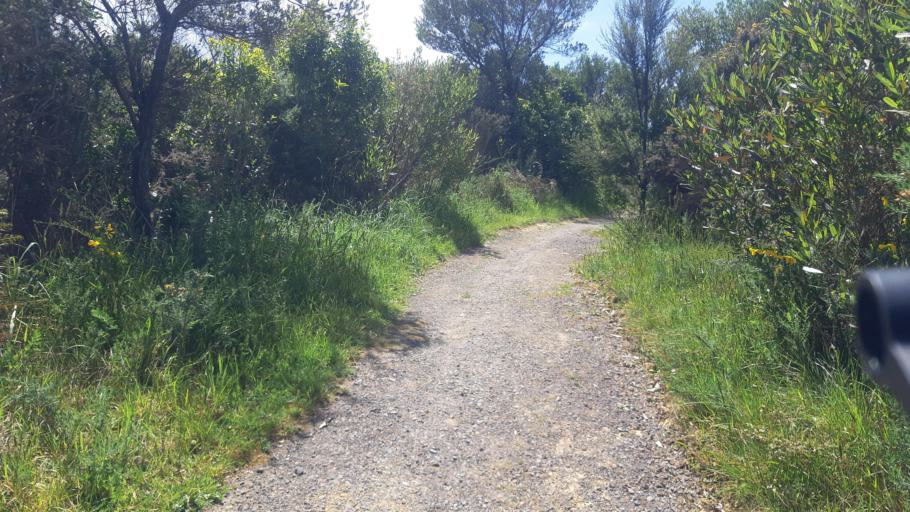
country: NZ
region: Marlborough
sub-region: Marlborough District
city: Picton
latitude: -41.2718
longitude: 174.0238
